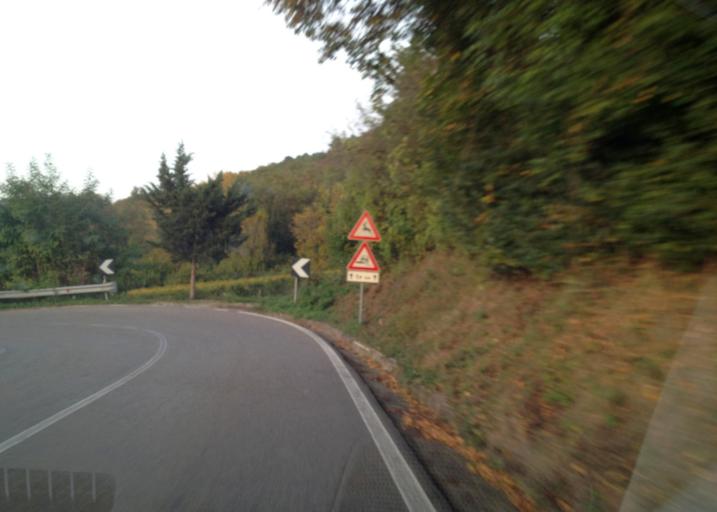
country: IT
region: Tuscany
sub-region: Province of Florence
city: Panzano in Chianti
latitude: 43.5104
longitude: 11.2927
